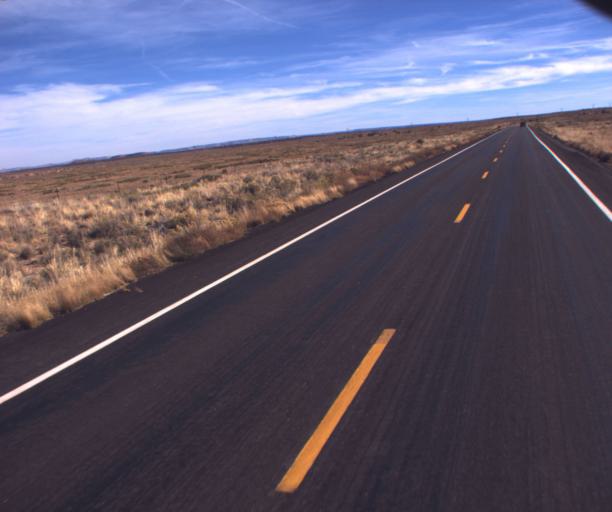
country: US
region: Arizona
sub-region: Coconino County
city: Kaibito
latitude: 36.6171
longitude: -110.9759
